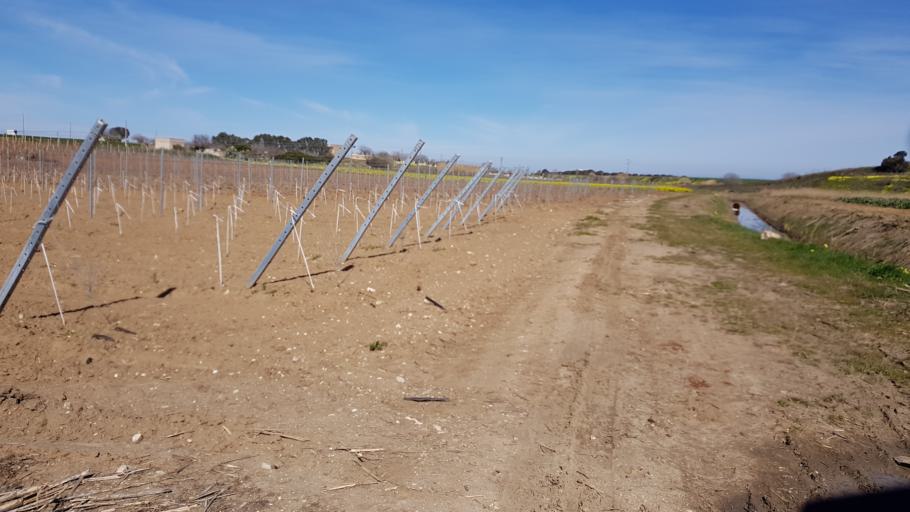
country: IT
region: Apulia
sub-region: Provincia di Brindisi
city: La Rosa
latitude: 40.6015
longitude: 17.9306
